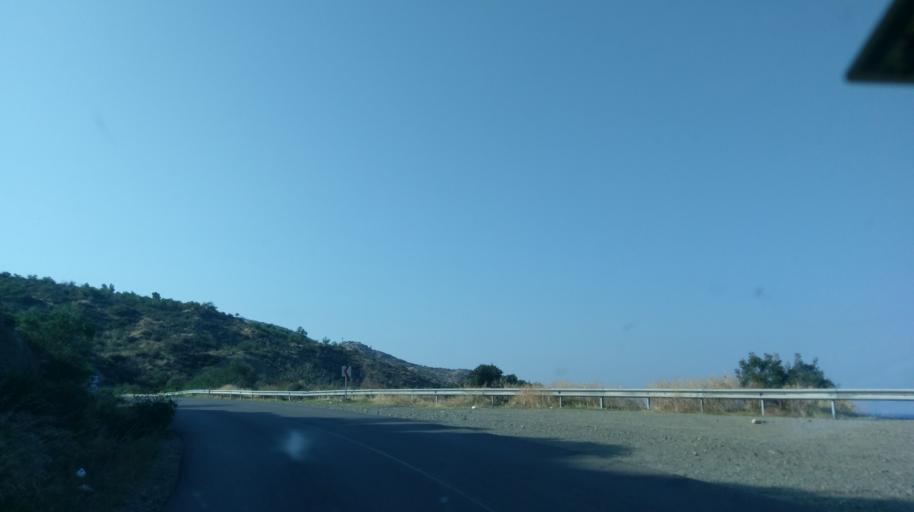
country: CY
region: Lefkosia
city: Lefka
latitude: 35.1513
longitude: 32.7947
